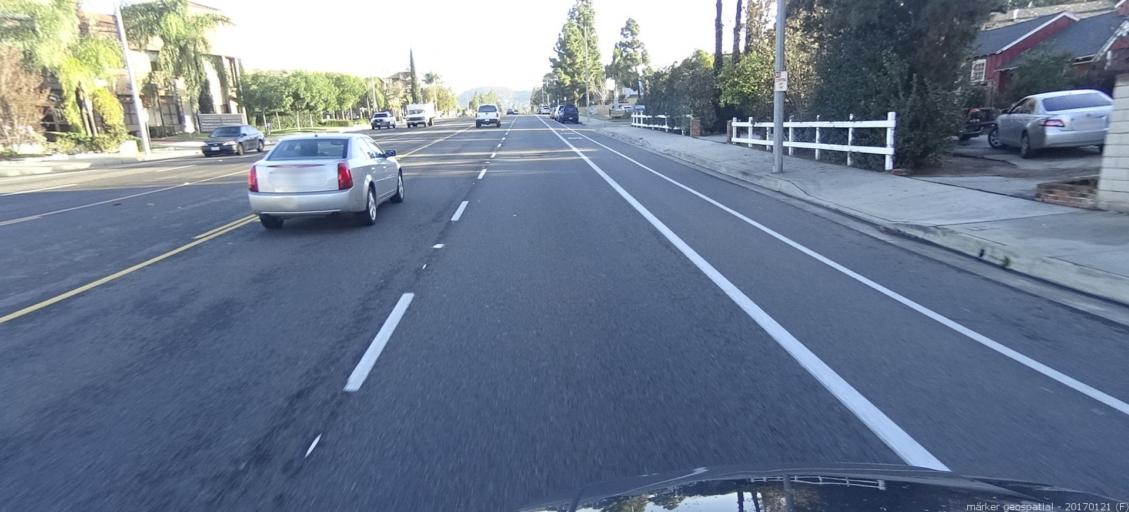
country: US
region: California
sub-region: Orange County
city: Tustin
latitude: 33.7511
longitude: -117.8091
